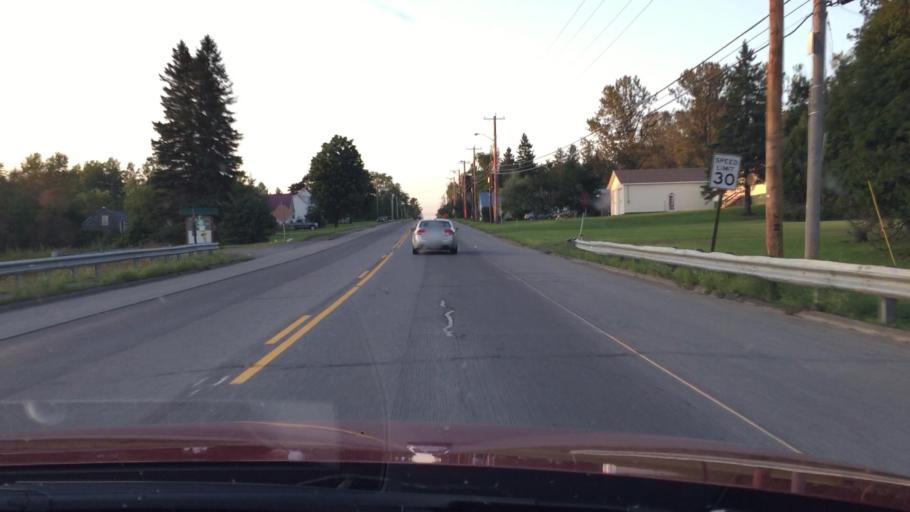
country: US
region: Maine
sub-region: Aroostook County
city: Houlton
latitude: 46.3123
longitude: -67.8413
